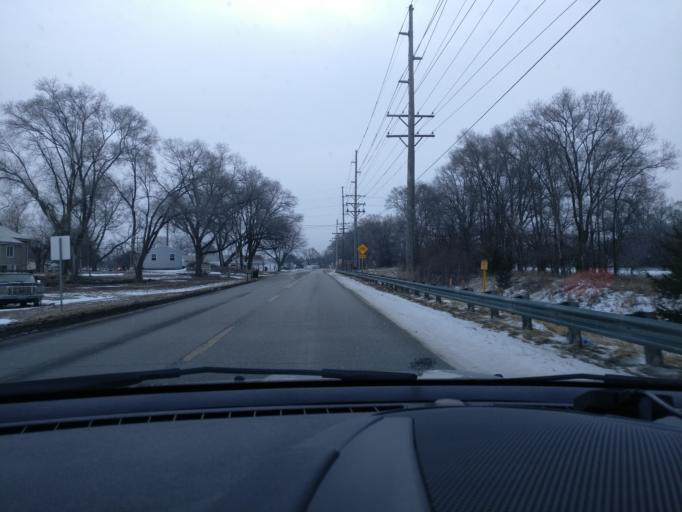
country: US
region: Nebraska
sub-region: Dodge County
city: Fremont
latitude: 41.4384
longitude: -96.5231
